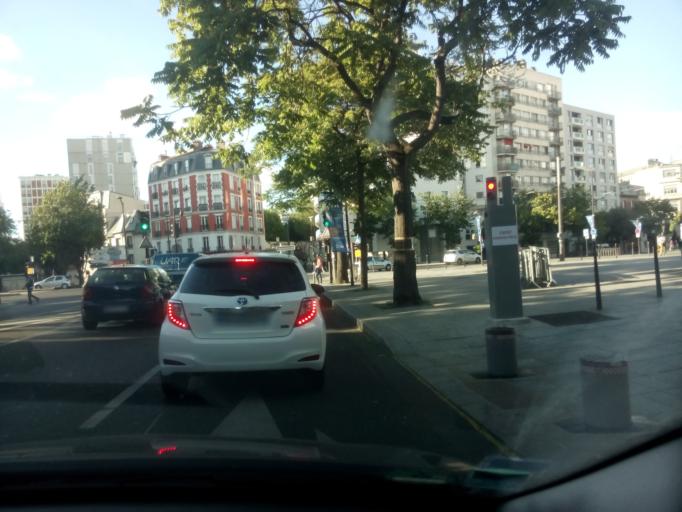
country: FR
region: Ile-de-France
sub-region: Departement du Val-de-Marne
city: Gentilly
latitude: 48.8191
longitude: 2.3445
